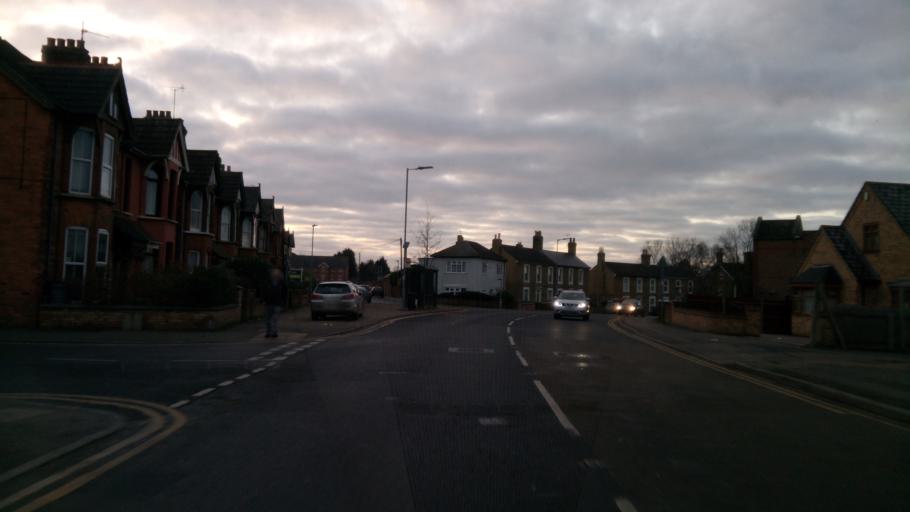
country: GB
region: England
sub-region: Peterborough
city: Peterborough
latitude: 52.5594
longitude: -0.2391
